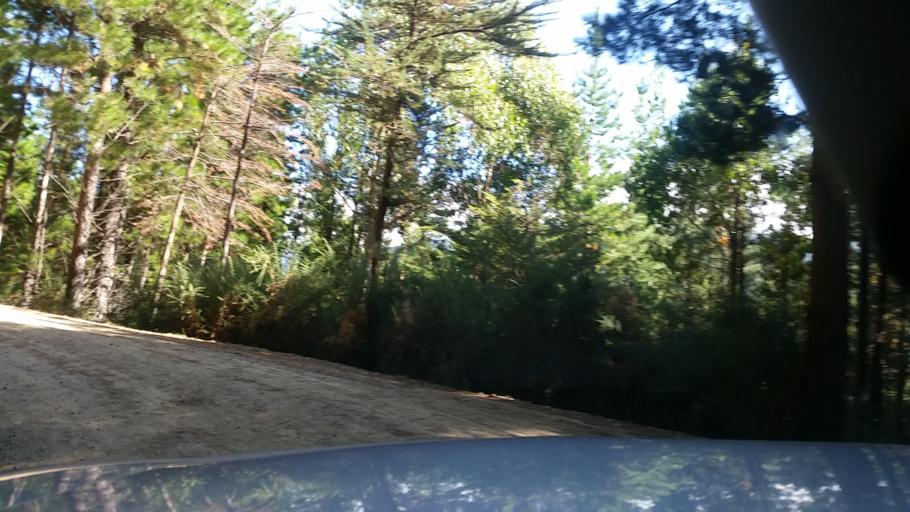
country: NZ
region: Marlborough
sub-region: Marlborough District
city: Picton
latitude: -41.2981
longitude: 174.1827
